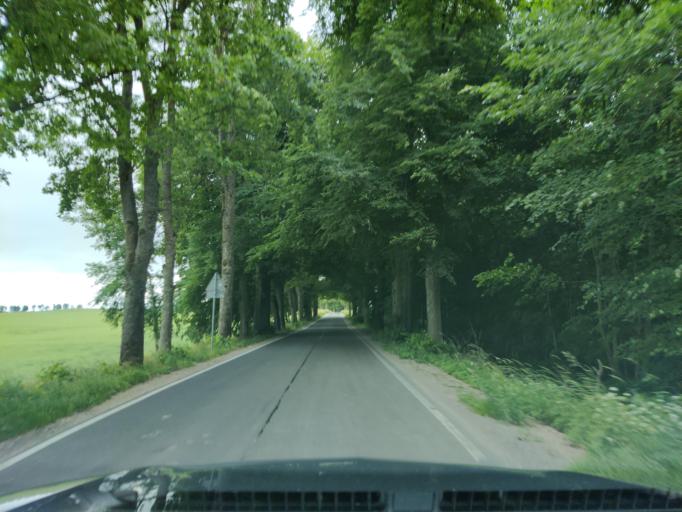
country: PL
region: Warmian-Masurian Voivodeship
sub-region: Powiat gizycki
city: Ryn
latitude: 53.9102
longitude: 21.5606
